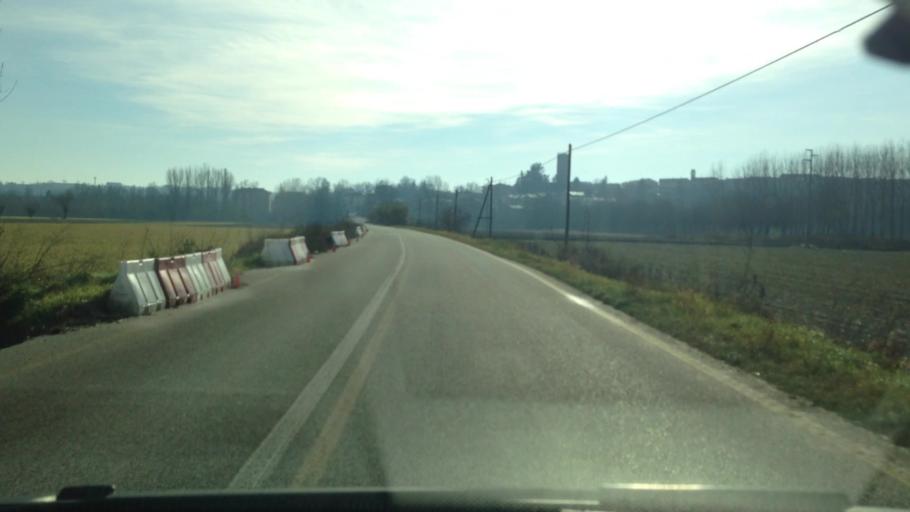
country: IT
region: Piedmont
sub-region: Provincia di Alessandria
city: Masio
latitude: 44.8768
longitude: 8.4094
